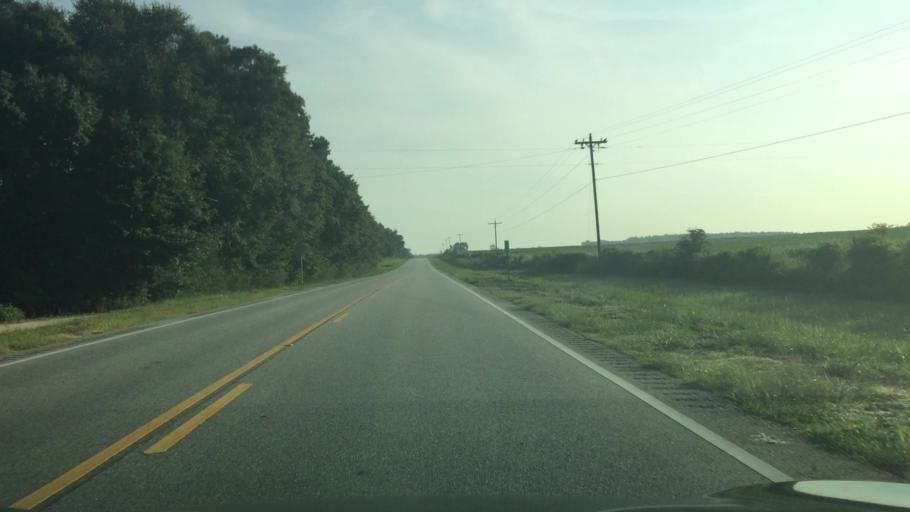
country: US
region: Alabama
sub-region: Covington County
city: Andalusia
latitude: 31.1732
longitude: -86.4591
